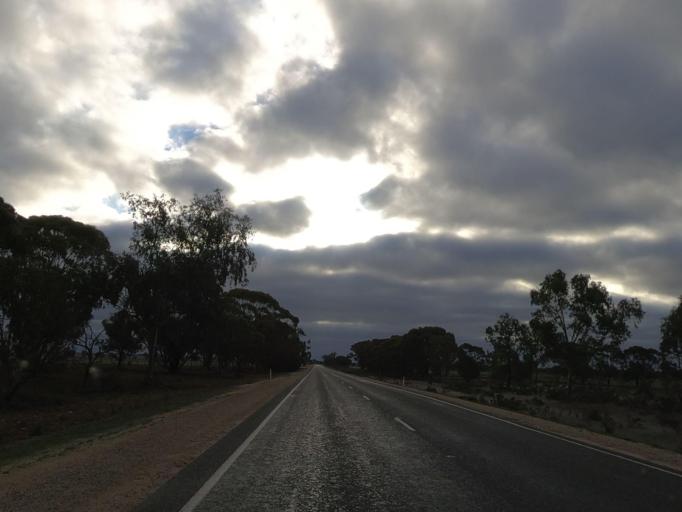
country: AU
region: Victoria
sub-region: Swan Hill
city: Swan Hill
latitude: -35.6576
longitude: 143.8532
